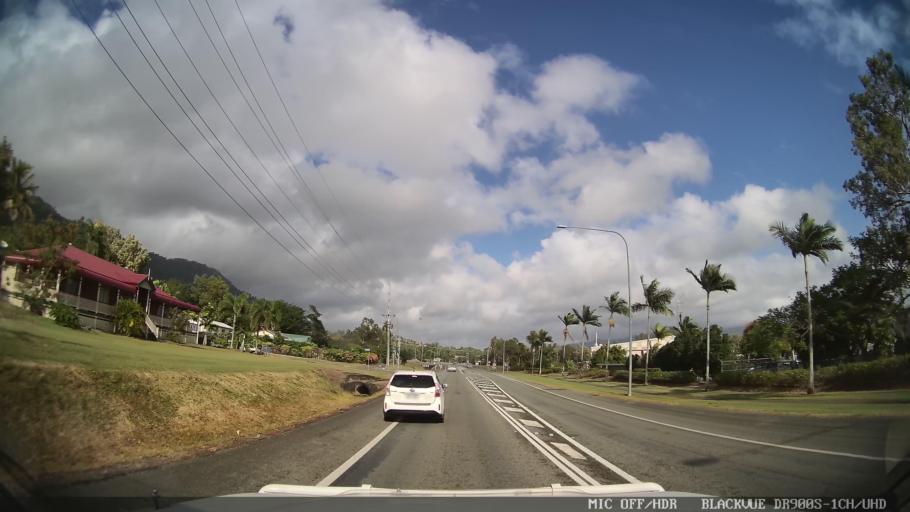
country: AU
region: Queensland
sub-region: Whitsunday
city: Proserpine
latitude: -20.2725
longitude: 148.7057
